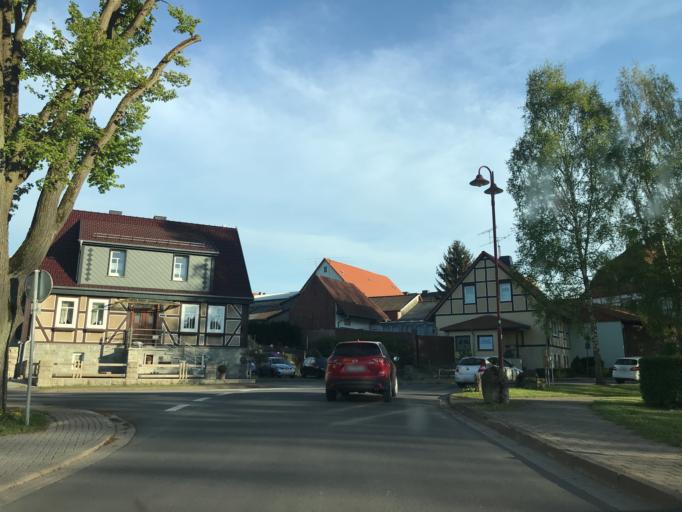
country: DE
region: Thuringia
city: Heuthen
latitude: 51.3344
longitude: 10.2264
